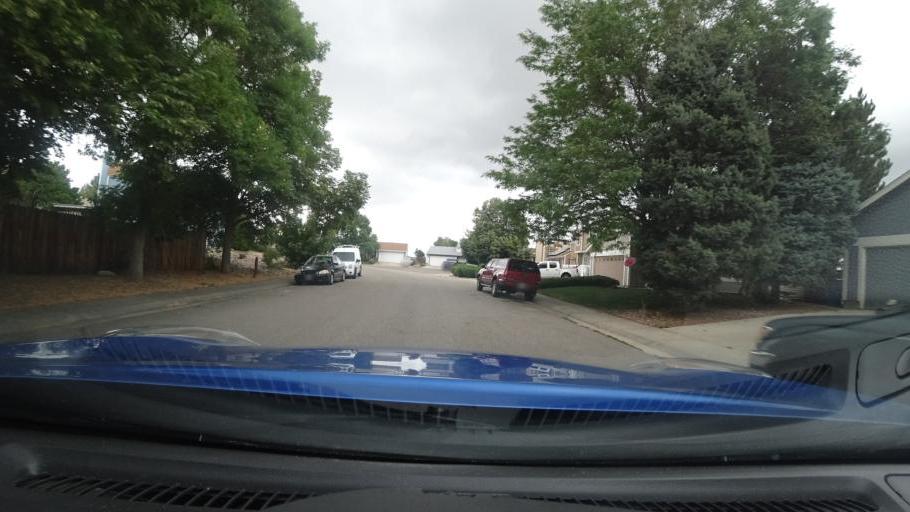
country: US
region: Colorado
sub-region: Adams County
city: Aurora
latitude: 39.7028
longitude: -104.8106
